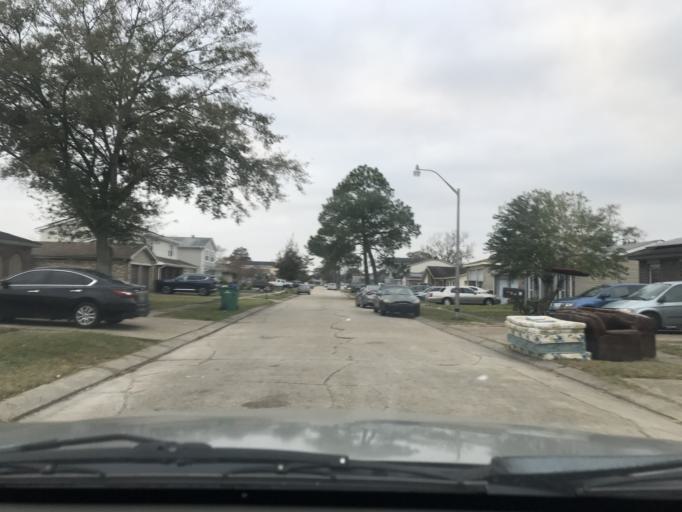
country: US
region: Louisiana
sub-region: Jefferson Parish
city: Woodmere
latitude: 29.8590
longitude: -90.0743
